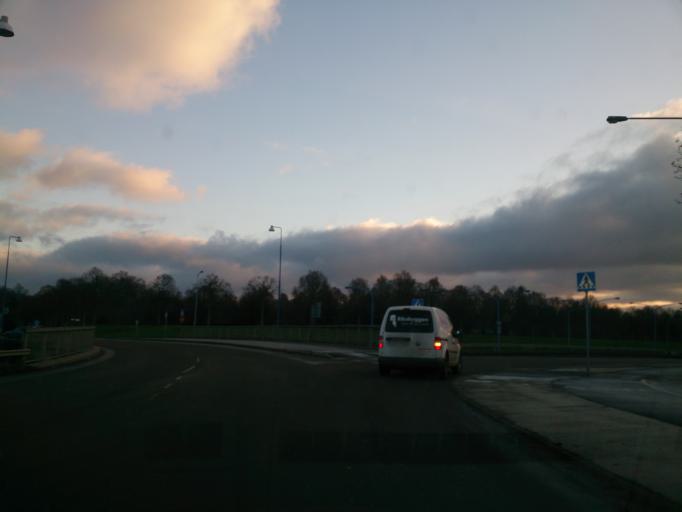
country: SE
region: OEstergoetland
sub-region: Norrkopings Kommun
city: Norrkoping
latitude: 58.5954
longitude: 16.1579
